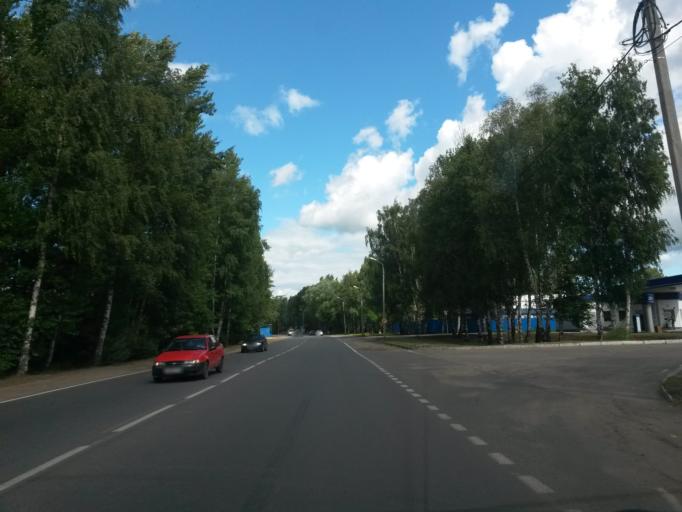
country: RU
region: Jaroslavl
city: Yaroslavl
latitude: 57.6539
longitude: 39.9077
